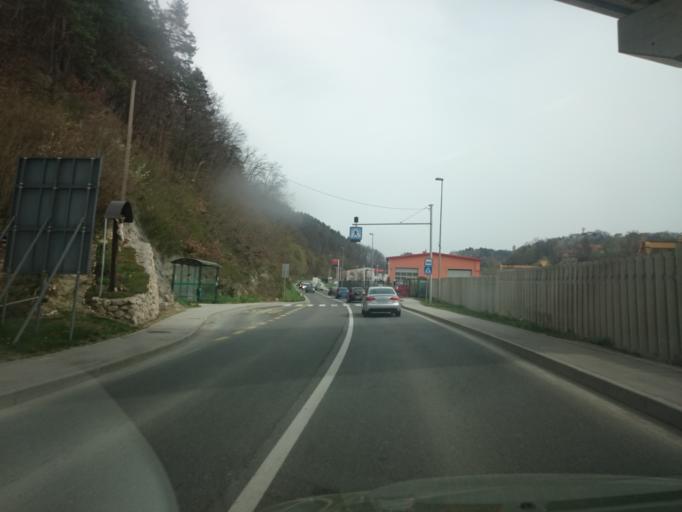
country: SI
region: Store
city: Store
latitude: 46.2245
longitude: 15.3104
